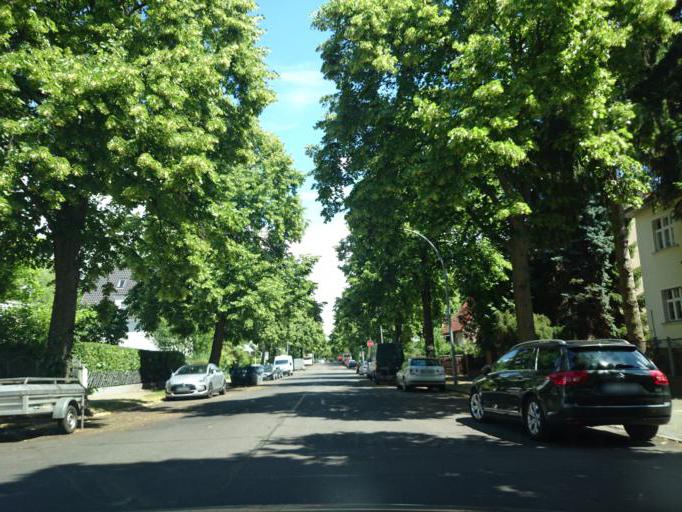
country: DE
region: Berlin
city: Lankwitz
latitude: 52.4197
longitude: 13.3300
